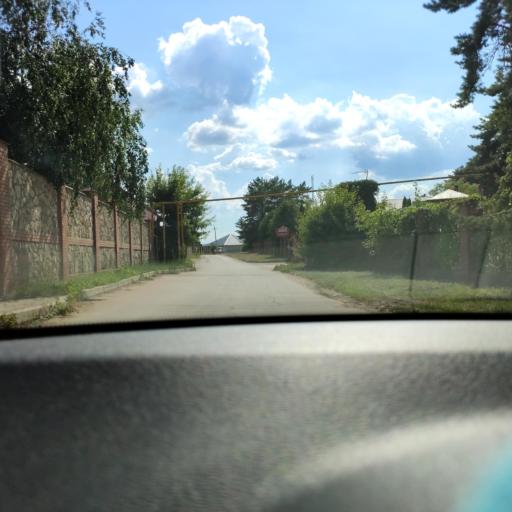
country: RU
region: Samara
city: Volzhskiy
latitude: 53.4431
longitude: 50.1744
